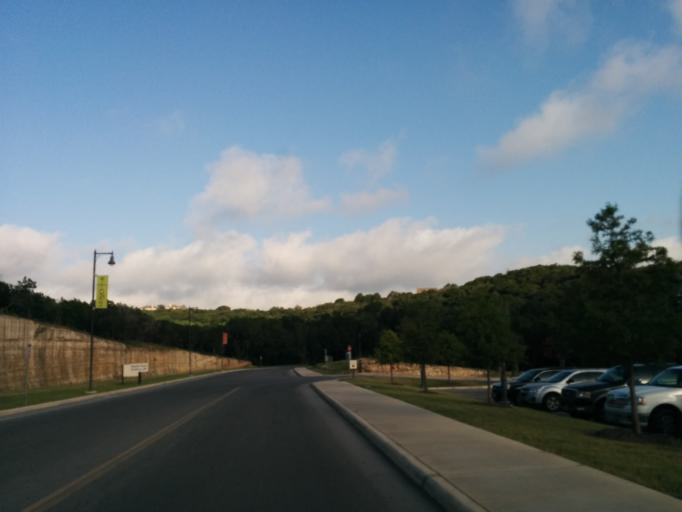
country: US
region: Texas
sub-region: Bexar County
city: Cross Mountain
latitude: 29.6112
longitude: -98.6087
